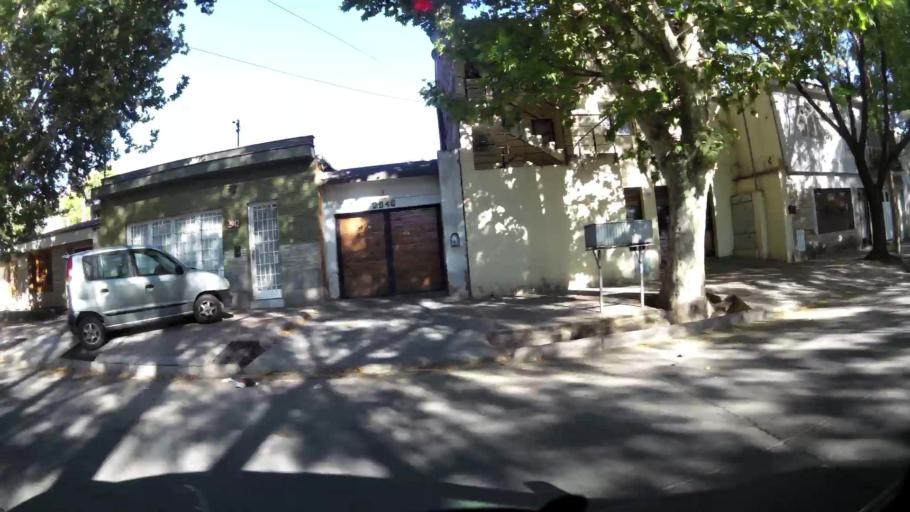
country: AR
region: Mendoza
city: Las Heras
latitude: -32.8683
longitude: -68.8363
